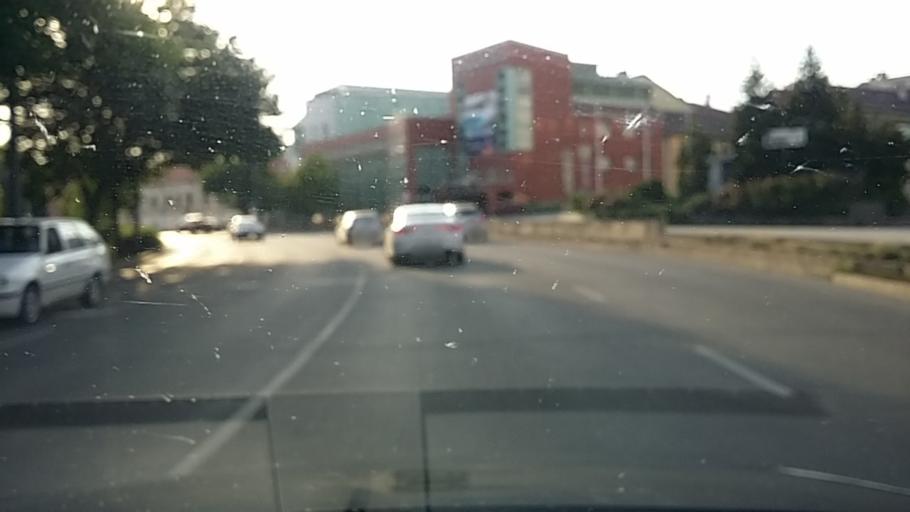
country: HU
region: Borsod-Abauj-Zemplen
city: Miskolc
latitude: 48.1015
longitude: 20.7830
